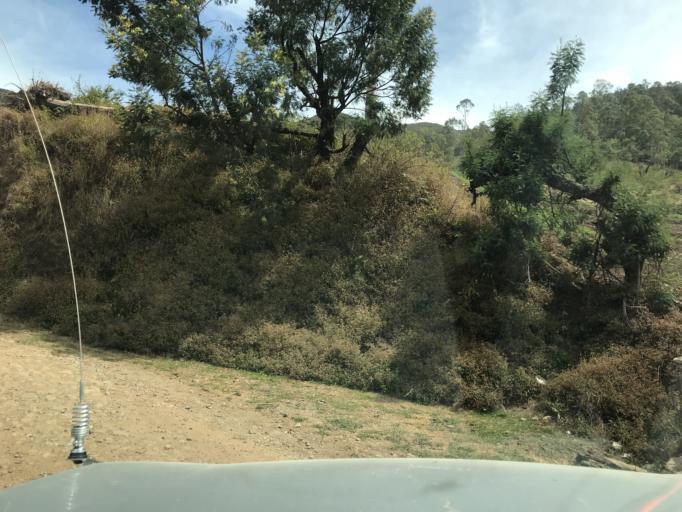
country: TL
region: Ainaro
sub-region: Ainaro
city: Ainaro
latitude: -8.8796
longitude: 125.5331
